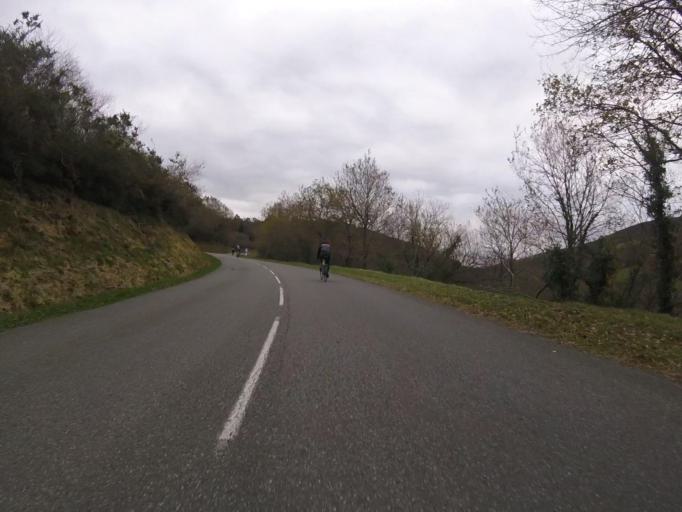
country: FR
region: Aquitaine
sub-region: Departement des Pyrenees-Atlantiques
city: Ascain
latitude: 43.3320
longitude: -1.6048
